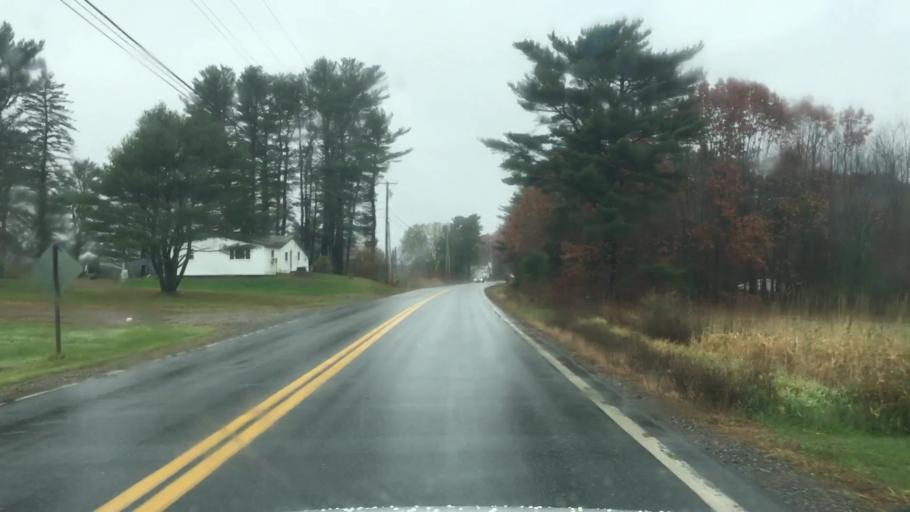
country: US
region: Maine
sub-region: Lincoln County
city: Waldoboro
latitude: 44.1266
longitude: -69.4131
